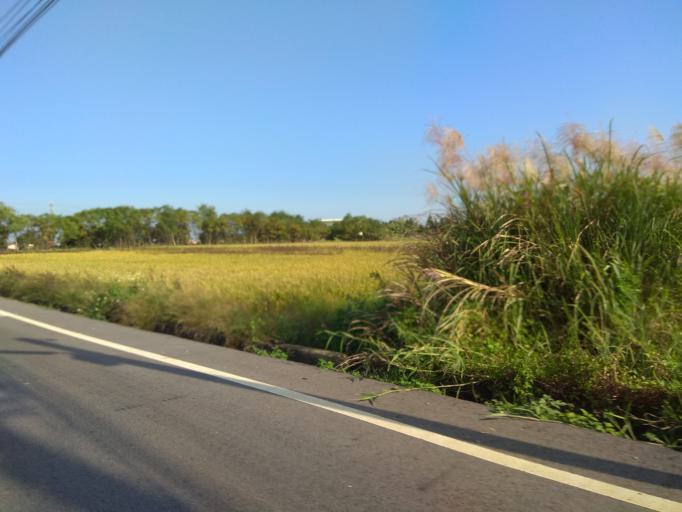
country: TW
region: Taiwan
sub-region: Hsinchu
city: Zhubei
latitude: 24.9893
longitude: 121.0743
